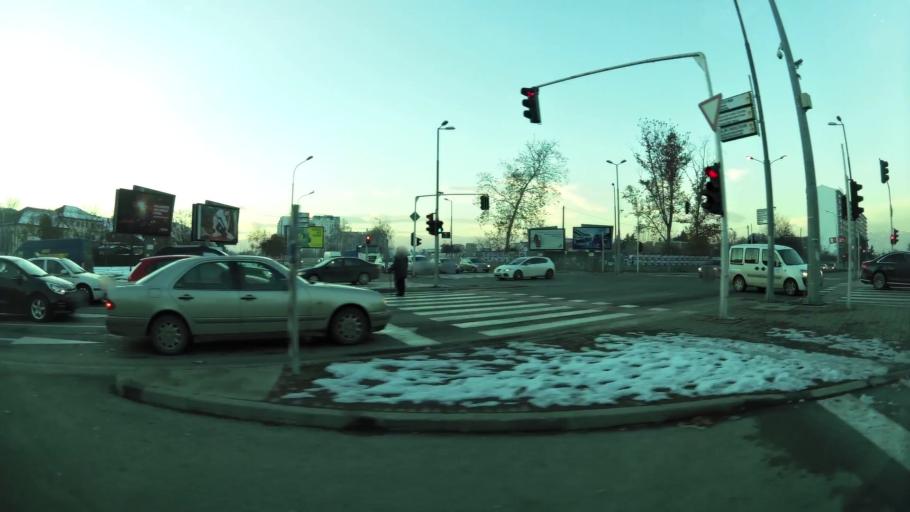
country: MK
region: Karpos
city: Skopje
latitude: 41.9963
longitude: 21.4037
